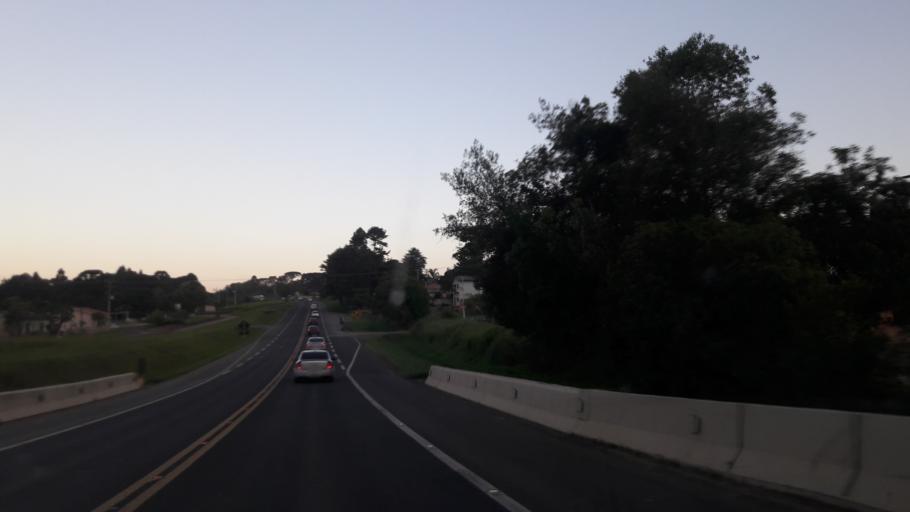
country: BR
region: Parana
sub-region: Palmeira
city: Palmeira
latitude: -25.4655
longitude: -50.2402
